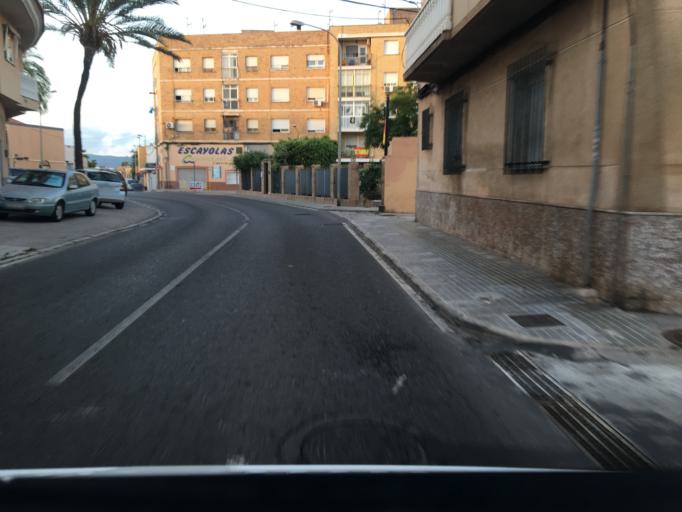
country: ES
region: Murcia
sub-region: Murcia
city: Cartagena
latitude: 37.6300
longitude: -0.9929
